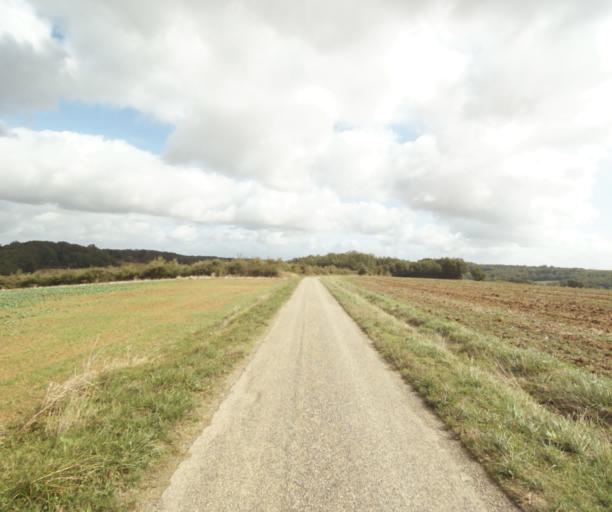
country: FR
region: Midi-Pyrenees
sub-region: Departement du Tarn-et-Garonne
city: Finhan
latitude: 43.8745
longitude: 1.1137
